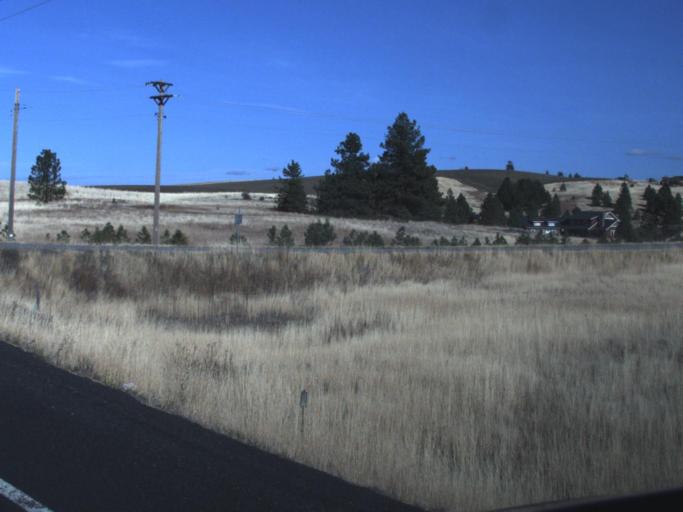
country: US
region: Washington
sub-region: Lincoln County
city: Davenport
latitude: 47.7881
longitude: -118.1736
